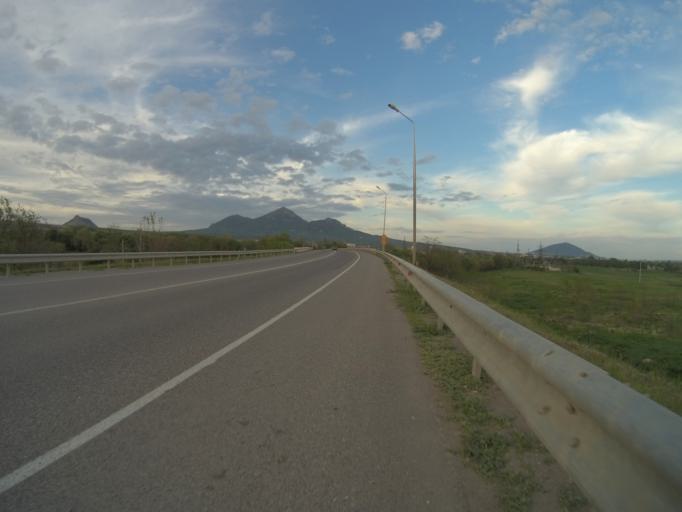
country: RU
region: Stavropol'skiy
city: Vinsady
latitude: 44.0552
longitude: 42.9542
